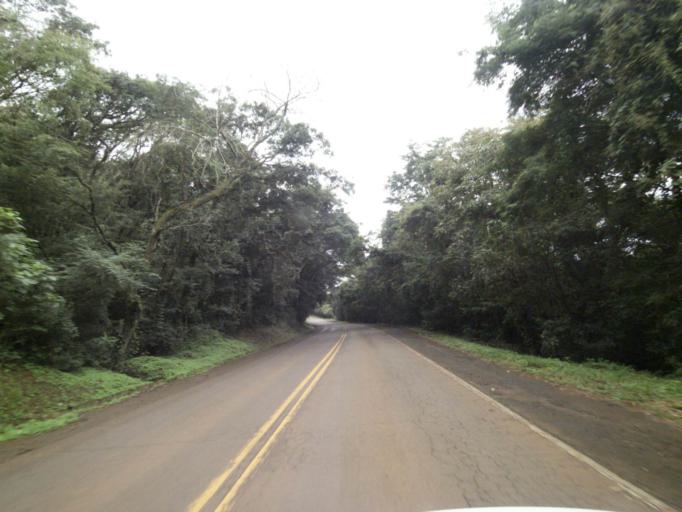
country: BR
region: Parana
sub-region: Marechal Candido Rondon
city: Marechal Candido Rondon
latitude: -24.7968
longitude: -54.2148
